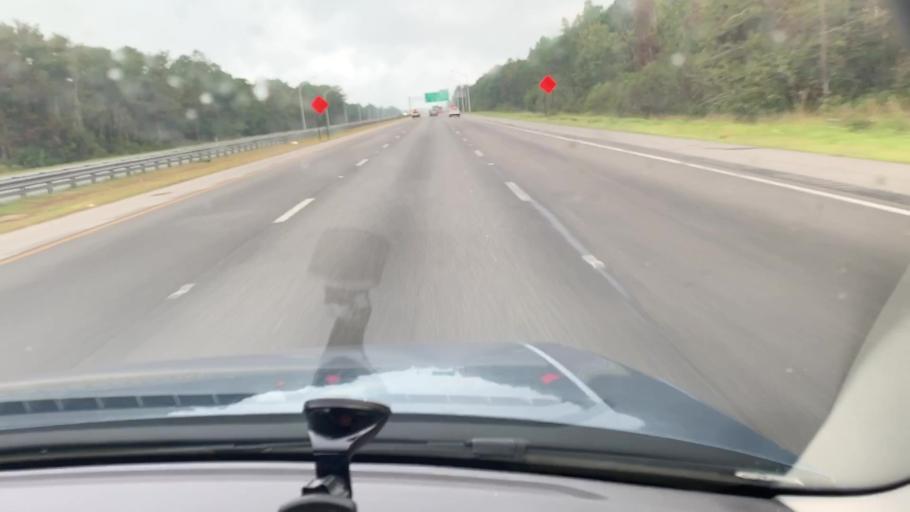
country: US
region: Florida
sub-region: Volusia County
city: South Daytona
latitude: 29.1366
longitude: -81.0648
